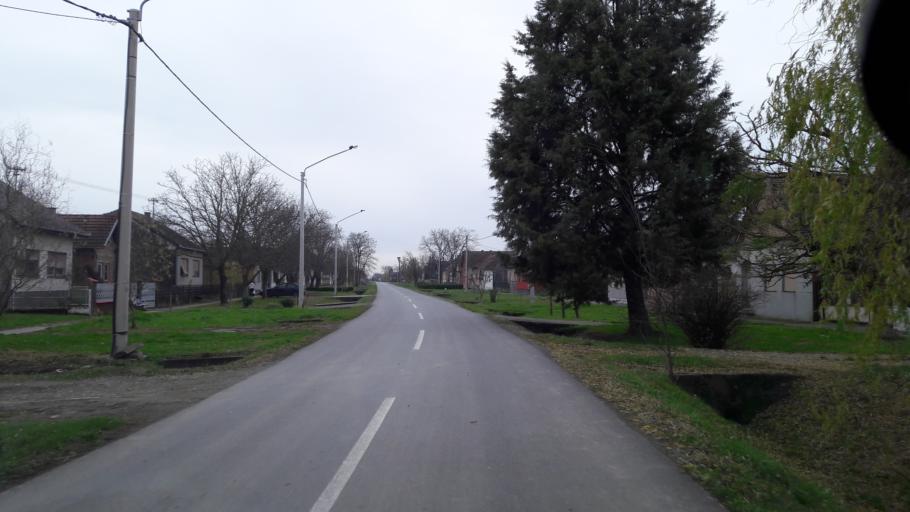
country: HR
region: Osjecko-Baranjska
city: Vladislavci
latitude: 45.4538
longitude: 18.5577
